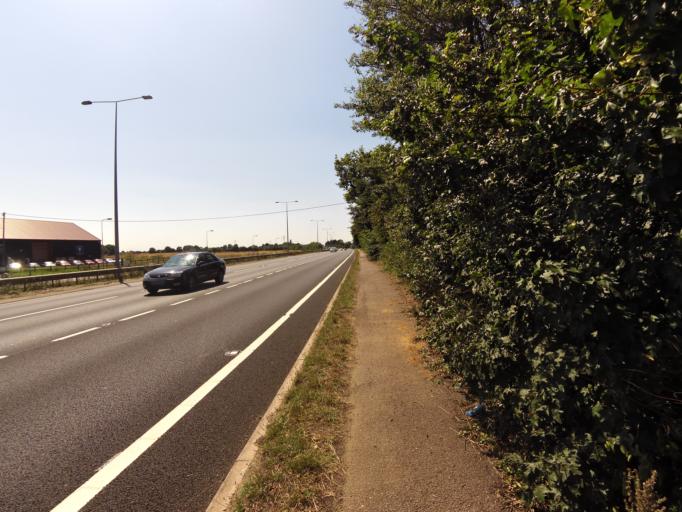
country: GB
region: England
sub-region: Suffolk
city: Capel Saint Mary
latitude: 52.0094
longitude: 1.0626
